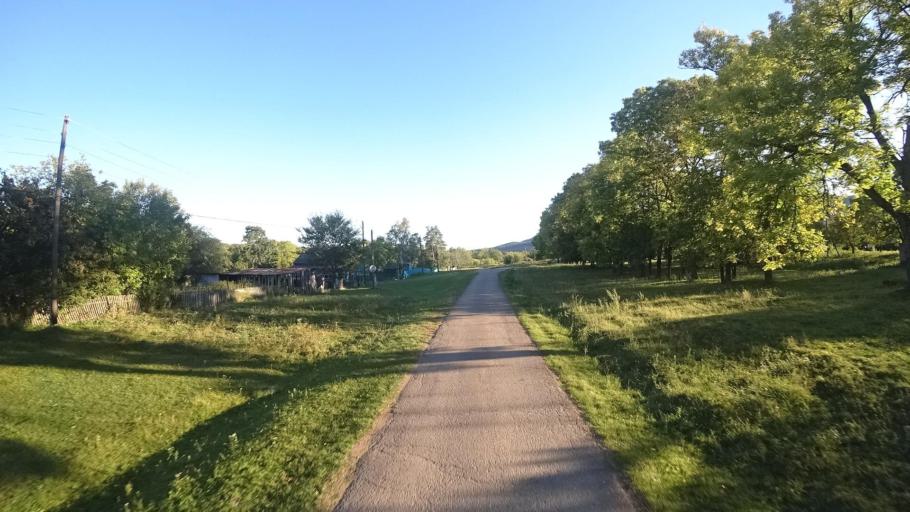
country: RU
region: Primorskiy
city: Kirovskiy
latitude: 44.8284
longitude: 133.5751
